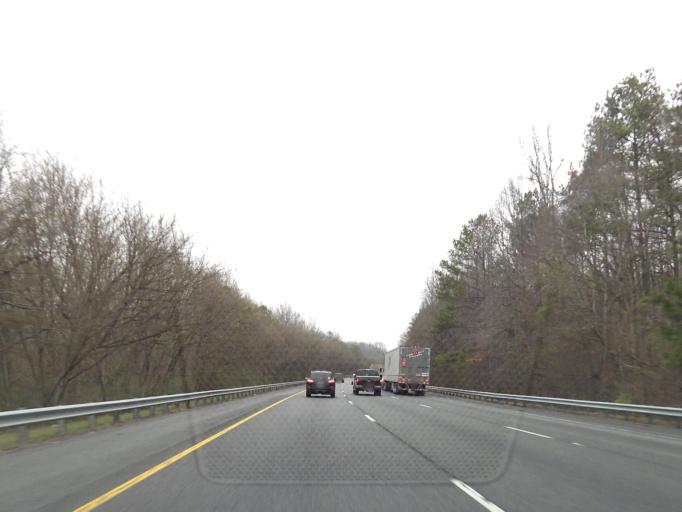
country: US
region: Georgia
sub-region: Monroe County
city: Forsyth
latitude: 33.0815
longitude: -83.9894
